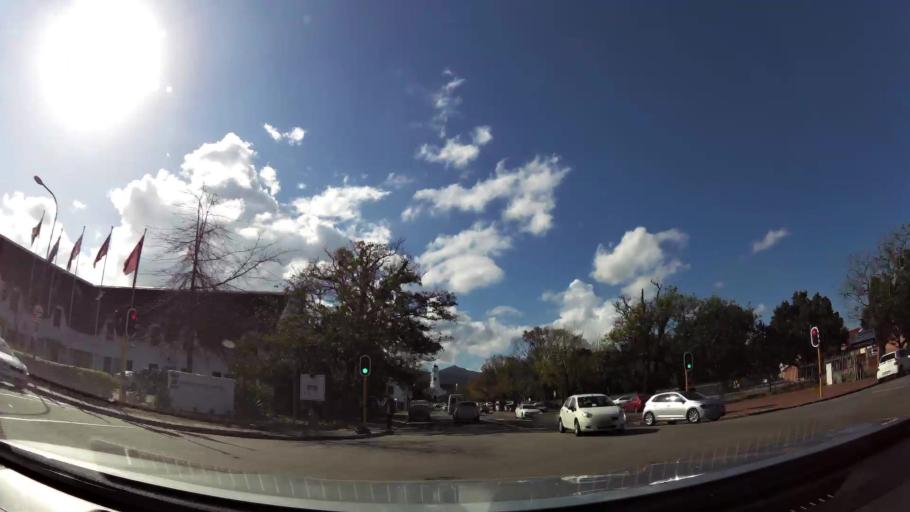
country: ZA
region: Western Cape
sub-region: Eden District Municipality
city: George
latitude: -33.9588
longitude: 22.4610
